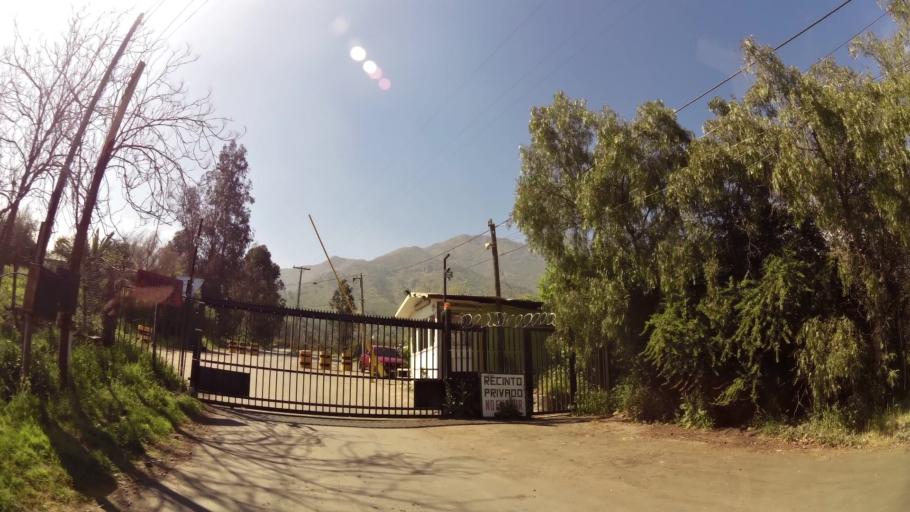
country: CL
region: Santiago Metropolitan
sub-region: Provincia de Santiago
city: Villa Presidente Frei, Nunoa, Santiago, Chile
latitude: -33.4477
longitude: -70.5155
